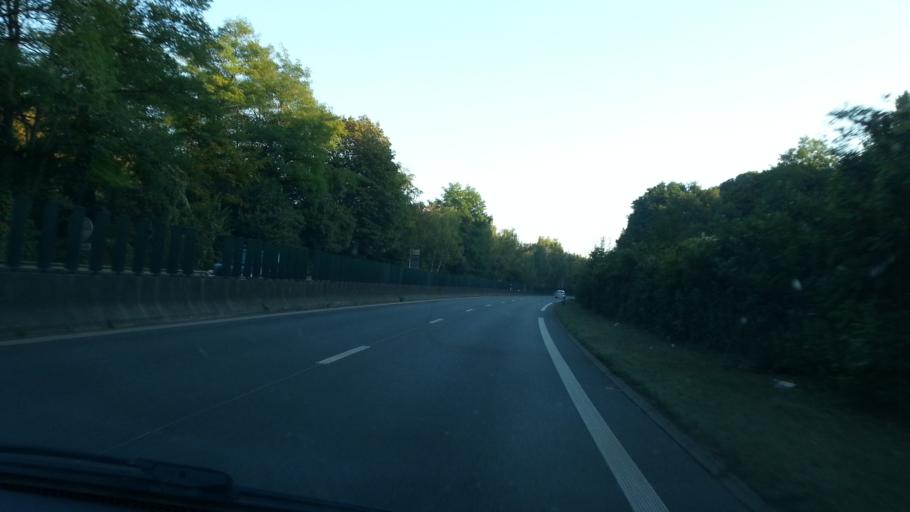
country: FR
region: Picardie
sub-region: Departement de l'Oise
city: Creil
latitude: 49.2601
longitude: 2.4910
